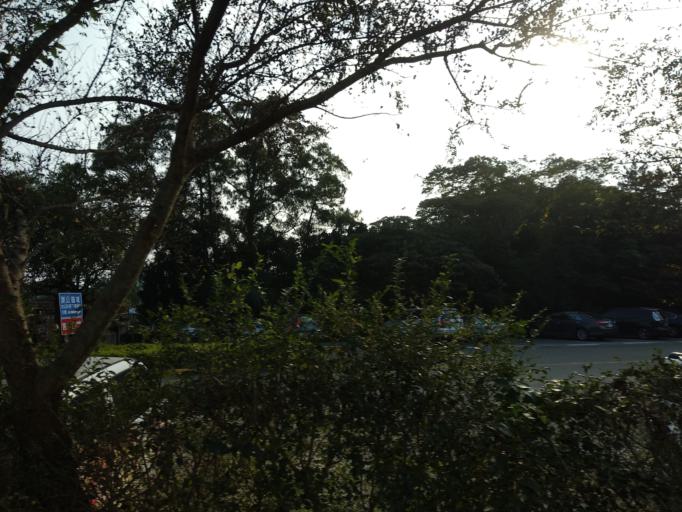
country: TW
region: Taiwan
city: Daxi
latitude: 24.8228
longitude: 121.1837
